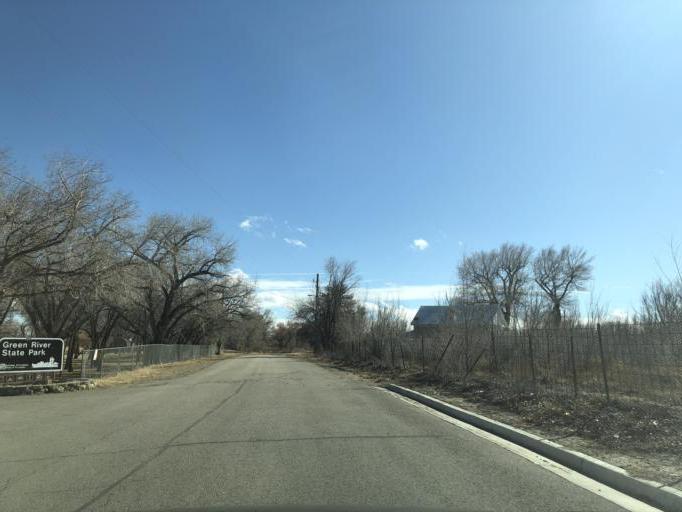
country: US
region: Utah
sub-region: Carbon County
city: East Carbon City
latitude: 38.9898
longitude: -110.1546
